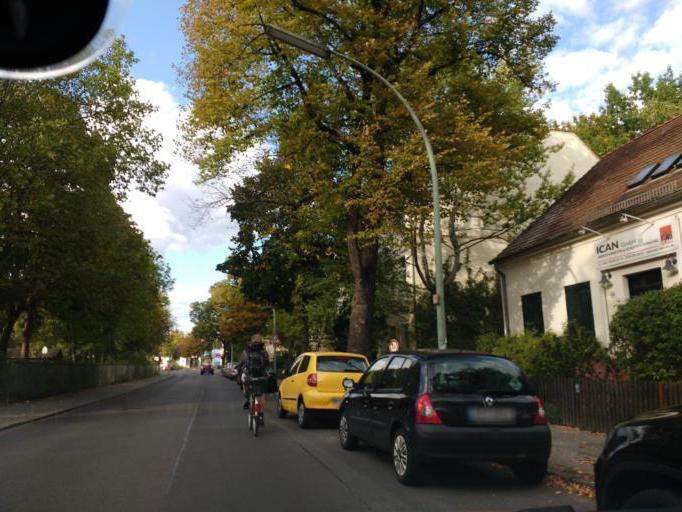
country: DE
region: Berlin
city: Britz
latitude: 52.4207
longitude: 13.4382
